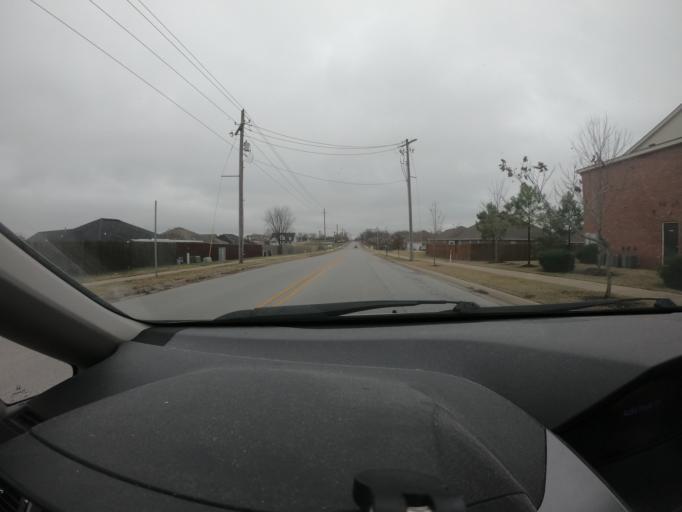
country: US
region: Arkansas
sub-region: Benton County
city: Bentonville
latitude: 36.3557
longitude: -94.2397
